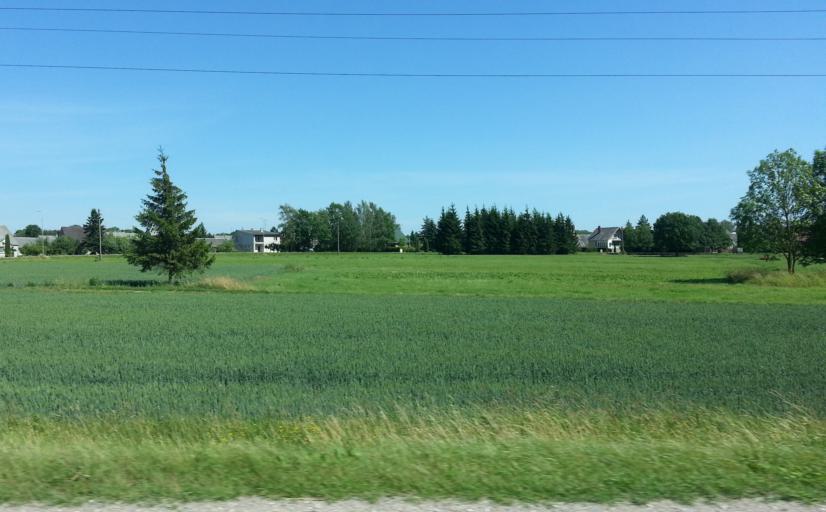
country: LT
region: Panevezys
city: Pasvalys
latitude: 56.0727
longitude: 24.4380
